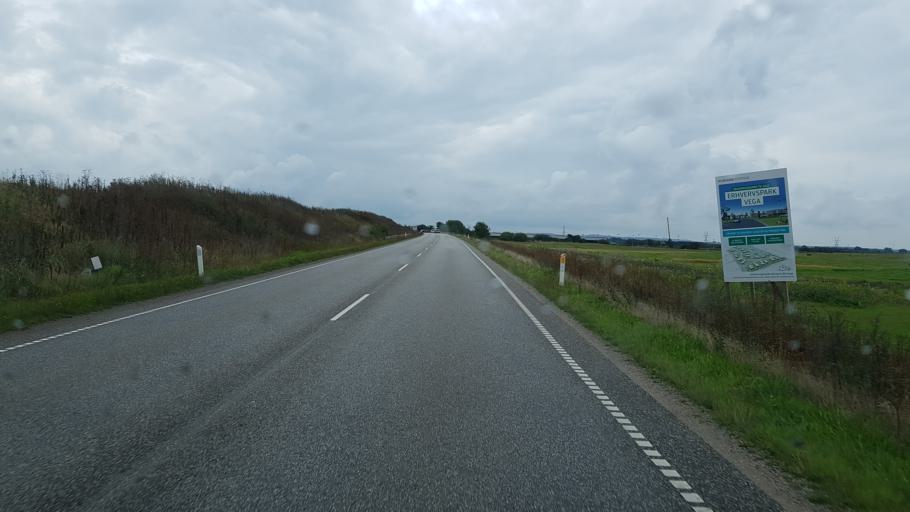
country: DK
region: Central Jutland
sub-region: Horsens Kommune
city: Horsens
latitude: 55.8937
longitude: 9.7581
